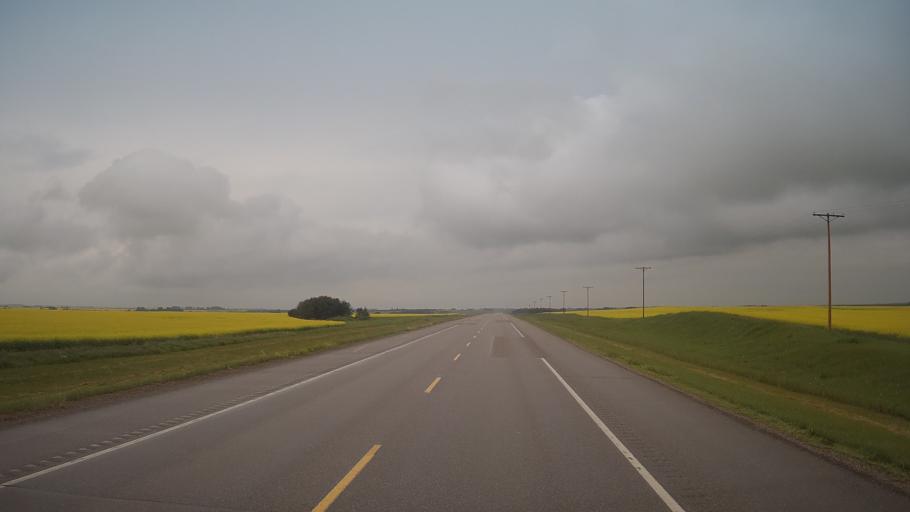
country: CA
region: Saskatchewan
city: Wilkie
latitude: 52.4279
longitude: -108.9132
